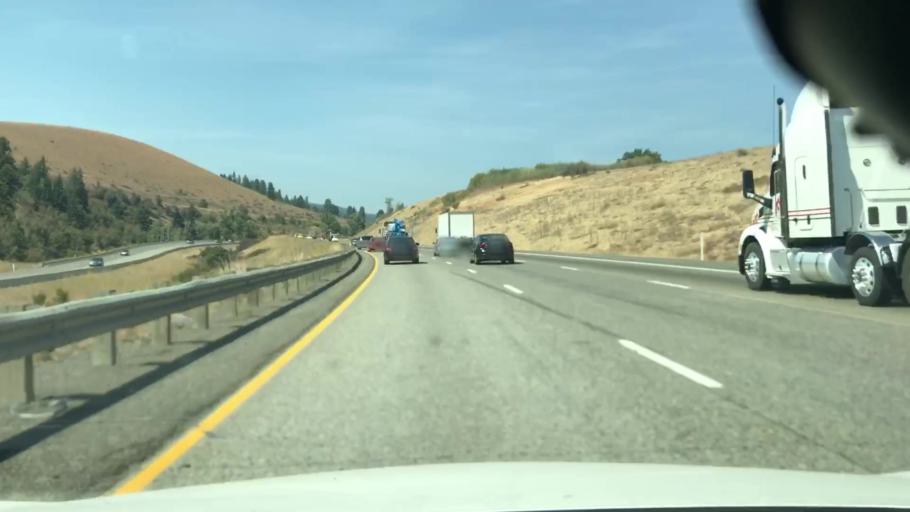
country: US
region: Washington
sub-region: Kittitas County
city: Cle Elum
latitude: 47.0893
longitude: -120.7470
